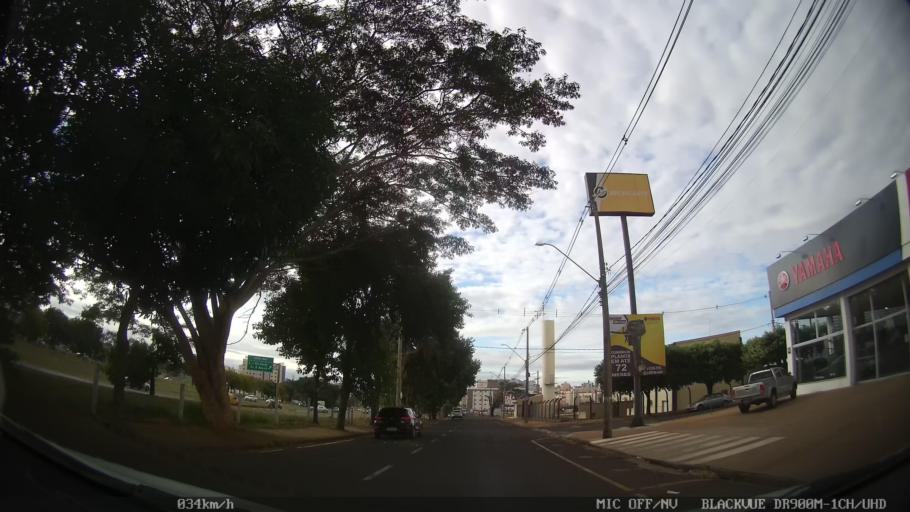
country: BR
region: Sao Paulo
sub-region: Sao Jose Do Rio Preto
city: Sao Jose do Rio Preto
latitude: -20.8252
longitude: -49.4087
